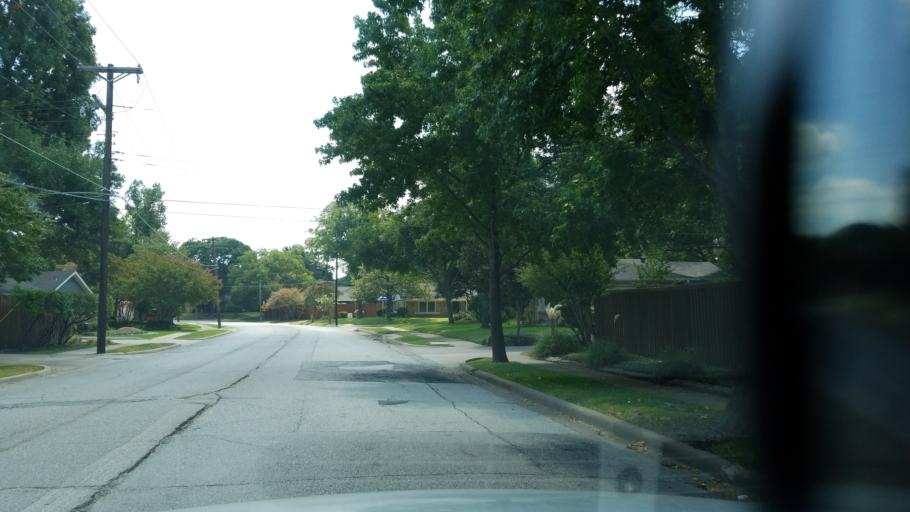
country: US
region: Texas
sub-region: Dallas County
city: Richardson
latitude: 32.9697
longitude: -96.7634
